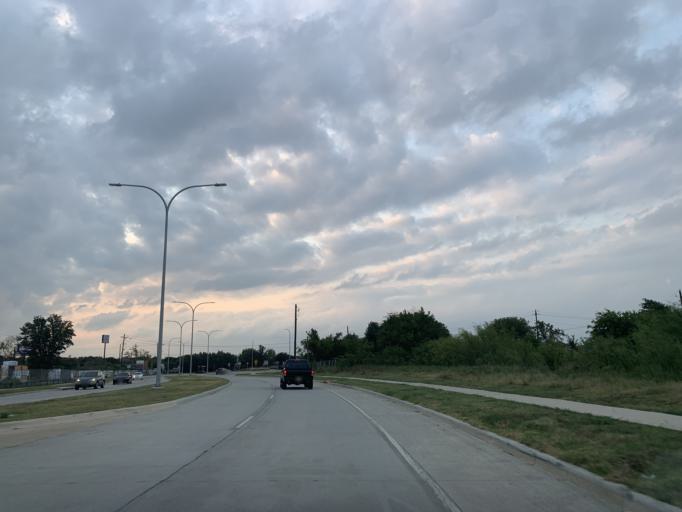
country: US
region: Texas
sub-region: Tarrant County
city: Keller
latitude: 32.9371
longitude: -97.2716
